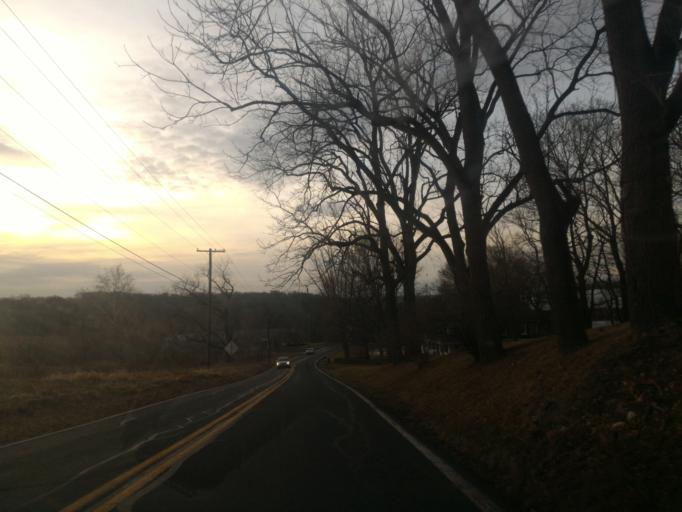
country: US
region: Pennsylvania
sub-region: York County
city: Jacobus
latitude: 39.8847
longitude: -76.6839
